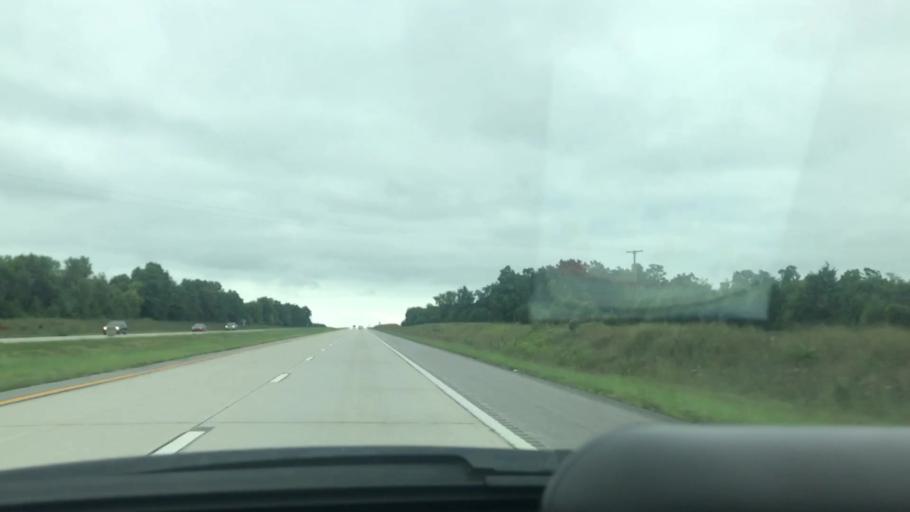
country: US
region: Missouri
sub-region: Greene County
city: Fair Grove
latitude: 37.4778
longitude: -93.1393
